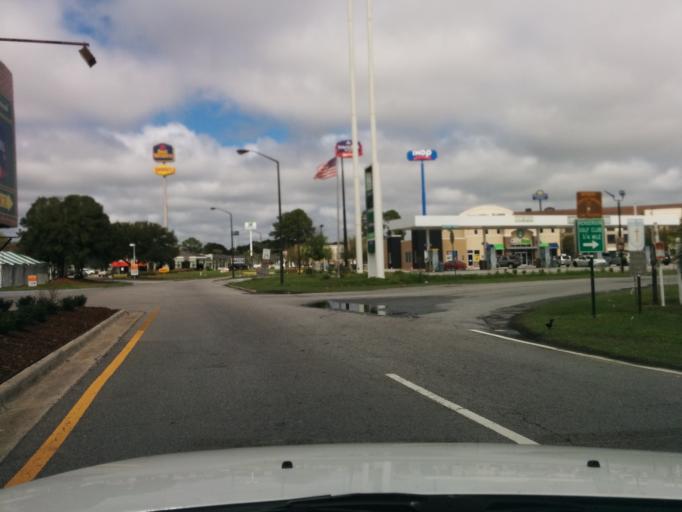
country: US
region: Georgia
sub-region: Chatham County
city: Georgetown
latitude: 32.0042
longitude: -81.2809
